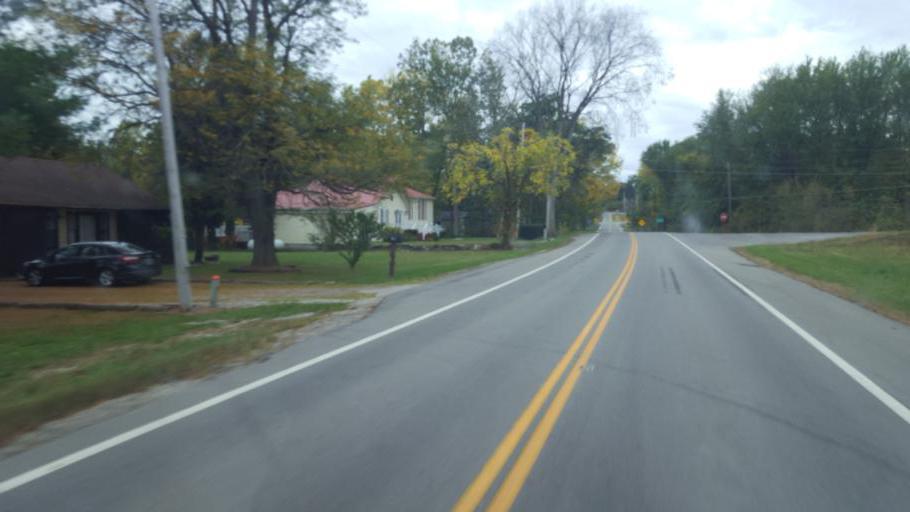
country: US
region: Ohio
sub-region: Huron County
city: Wakeman
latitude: 41.1984
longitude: -82.4084
